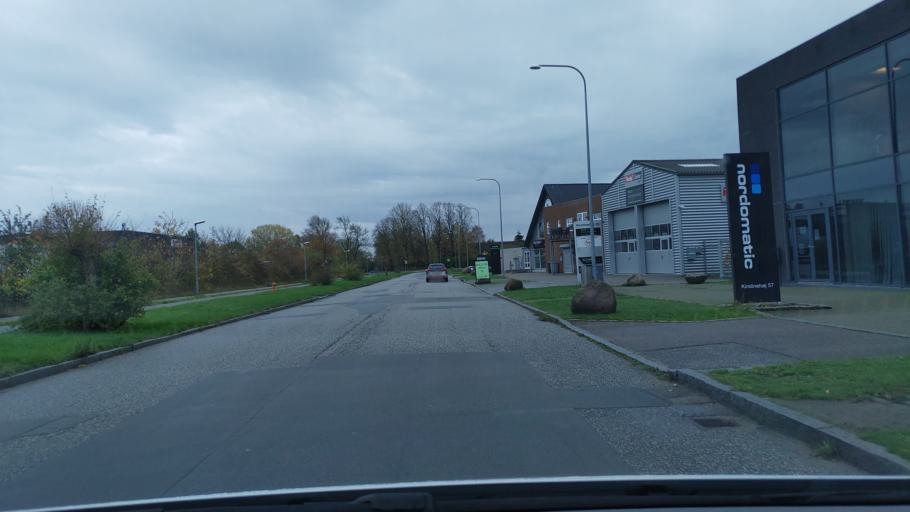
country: DK
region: Capital Region
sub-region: Tarnby Kommune
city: Tarnby
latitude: 55.6149
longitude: 12.6148
